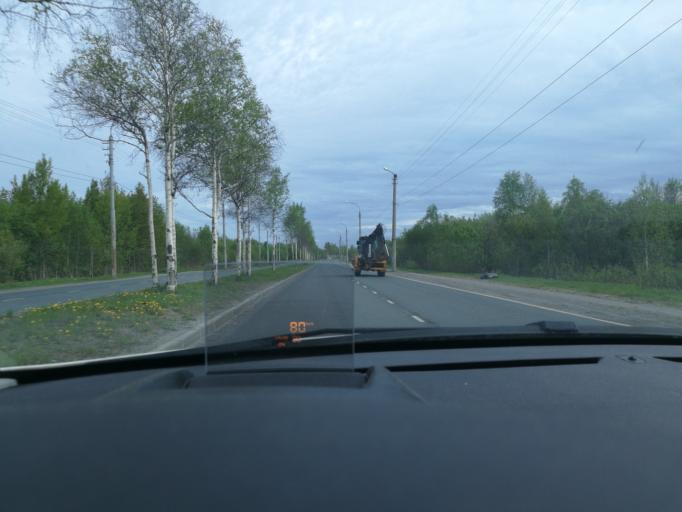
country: RU
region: Arkhangelskaya
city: Arkhangel'sk
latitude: 64.6060
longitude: 40.5248
